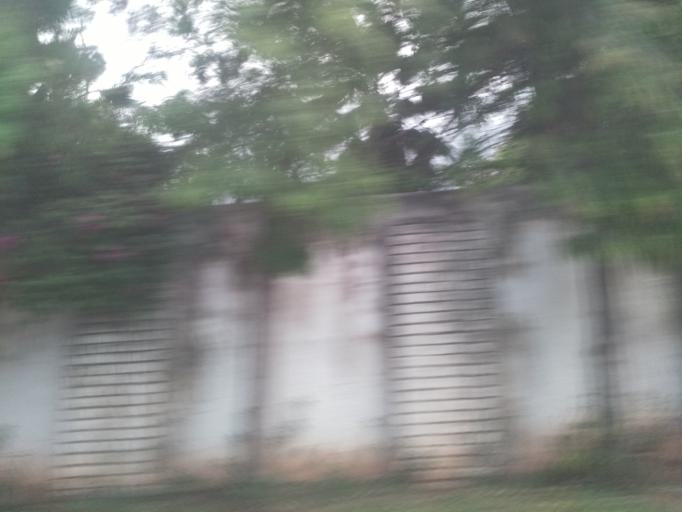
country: TZ
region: Dar es Salaam
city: Magomeni
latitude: -6.7565
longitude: 39.2789
